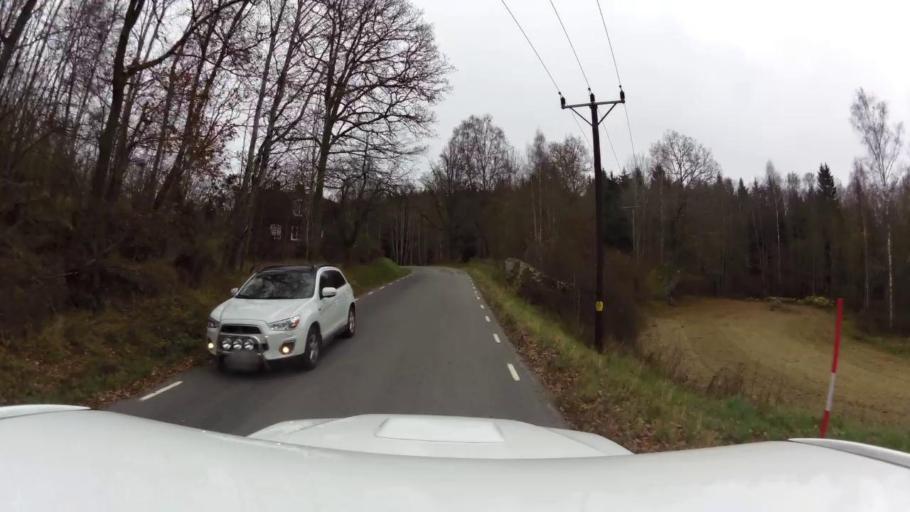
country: SE
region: OEstergoetland
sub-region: Kinda Kommun
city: Rimforsa
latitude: 58.1367
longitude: 15.6120
